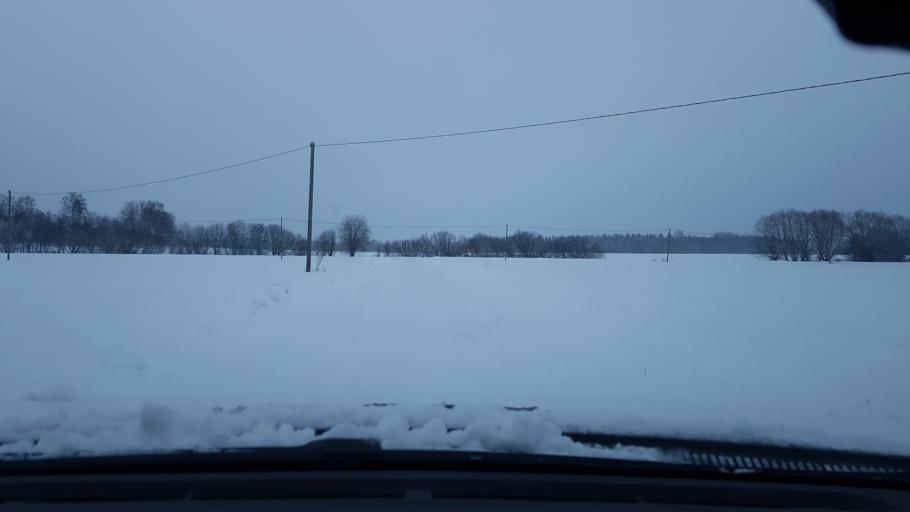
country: EE
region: Harju
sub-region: Anija vald
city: Kehra
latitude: 59.2495
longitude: 25.3541
